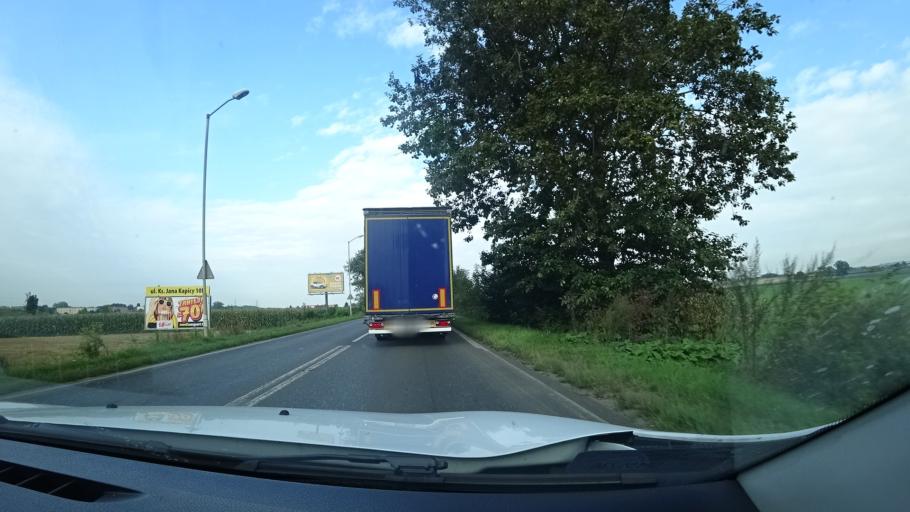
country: PL
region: Silesian Voivodeship
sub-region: Siemianowice Slaskie
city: Siemianowice Slaskie
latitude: 50.3312
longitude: 19.0088
